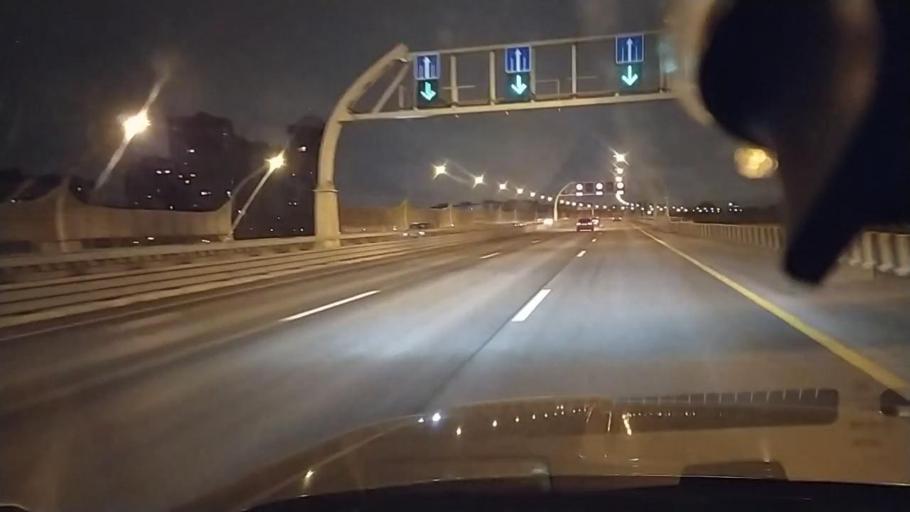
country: RU
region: Leningrad
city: Untolovo
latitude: 60.0240
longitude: 30.2127
